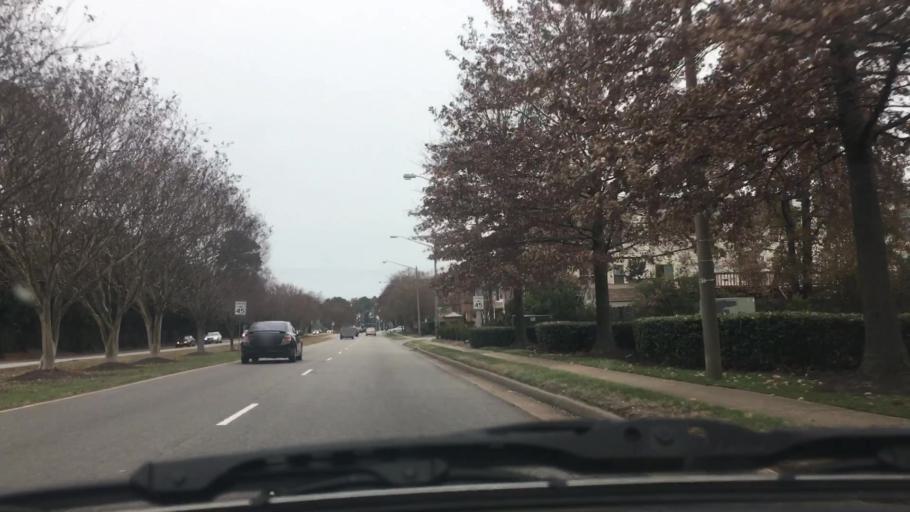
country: US
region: Virginia
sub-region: City of Chesapeake
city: Chesapeake
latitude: 36.8175
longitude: -76.1268
